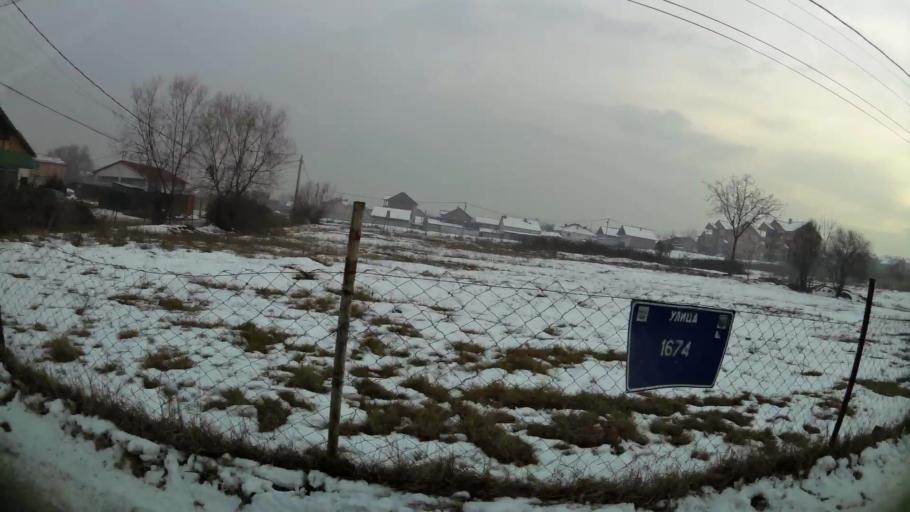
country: MK
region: Suto Orizari
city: Suto Orizare
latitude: 42.0375
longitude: 21.4195
